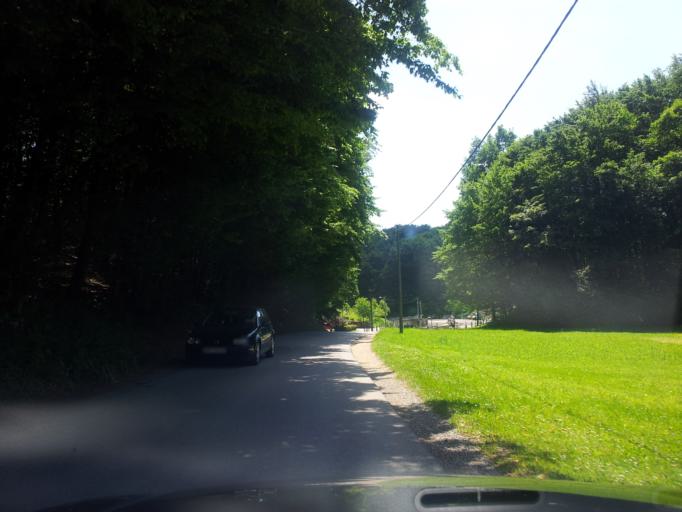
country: HR
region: Karlovacka
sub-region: Grad Karlovac
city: Karlovac
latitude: 45.4644
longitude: 15.4758
